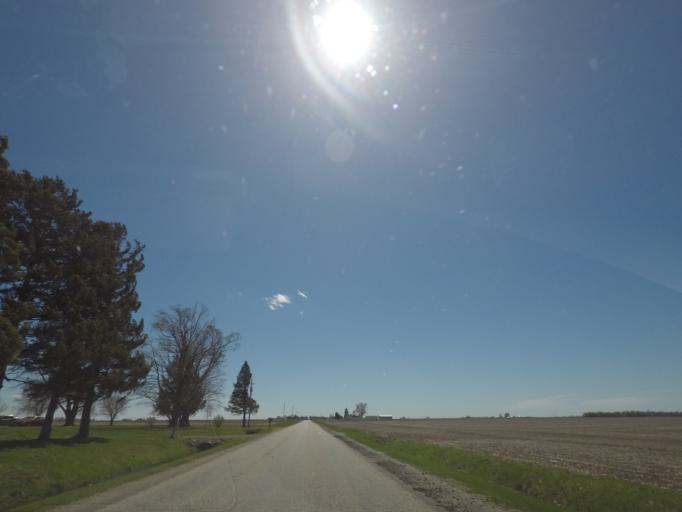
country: US
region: Illinois
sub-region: Logan County
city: Atlanta
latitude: 40.1705
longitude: -89.1937
